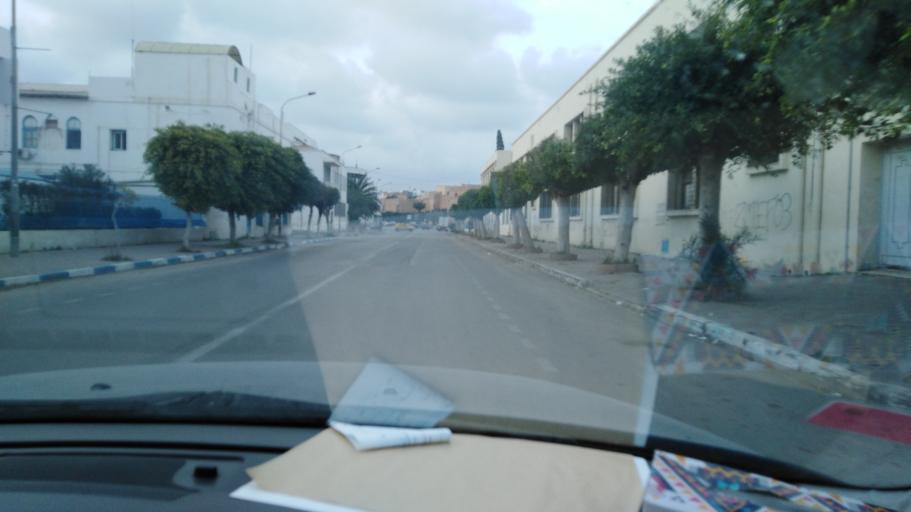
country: TN
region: Safaqis
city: Sfax
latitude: 34.7315
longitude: 10.7585
